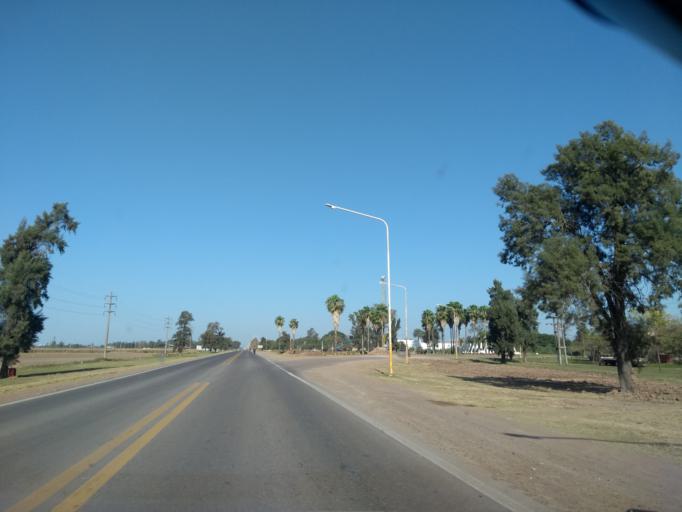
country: AR
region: Chaco
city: Presidencia Roque Saenz Pena
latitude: -26.7979
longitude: -60.4120
